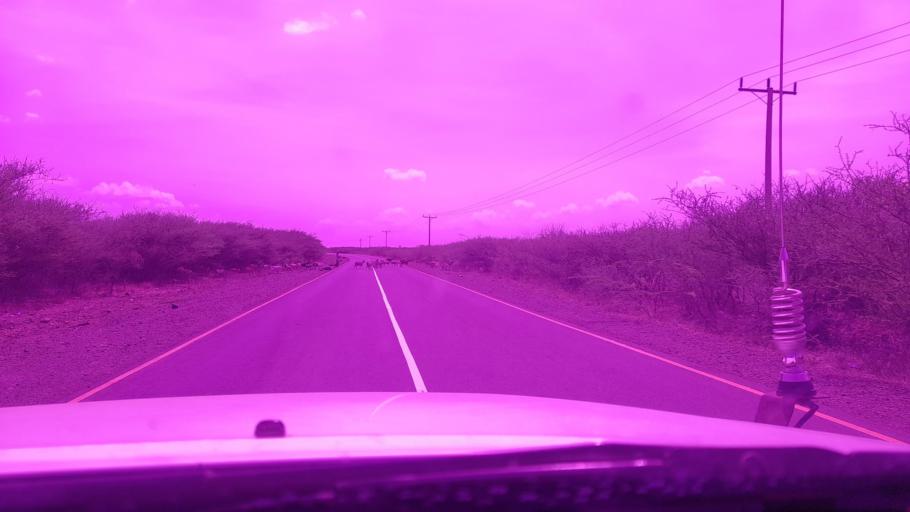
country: ET
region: Afar
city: Awash
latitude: 9.3521
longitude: 40.2997
